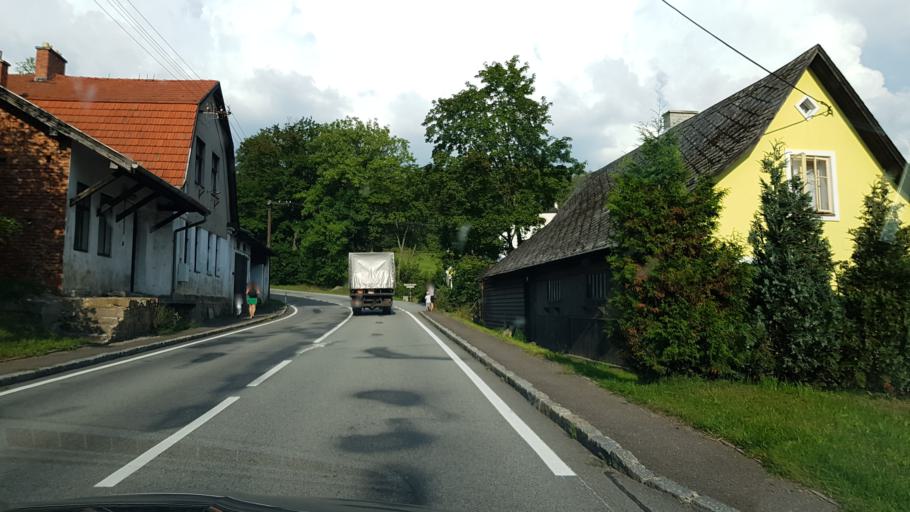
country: PL
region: Lower Silesian Voivodeship
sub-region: Powiat klodzki
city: Miedzylesie
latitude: 50.0981
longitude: 16.6296
